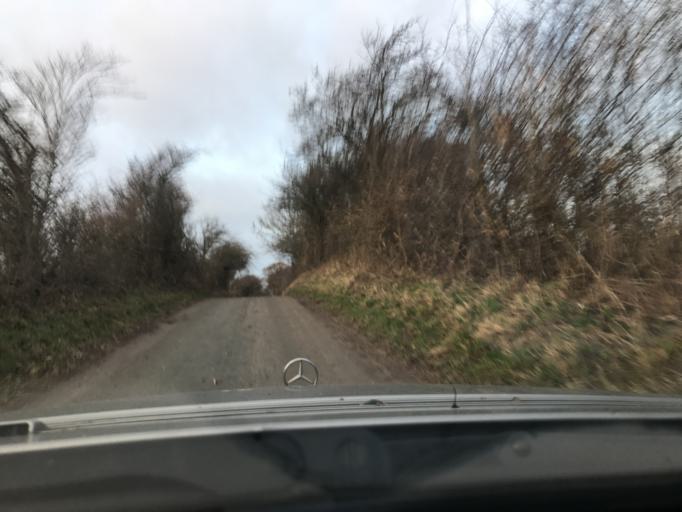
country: DK
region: South Denmark
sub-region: Sonderborg Kommune
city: Nordborg
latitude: 55.0596
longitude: 9.6709
